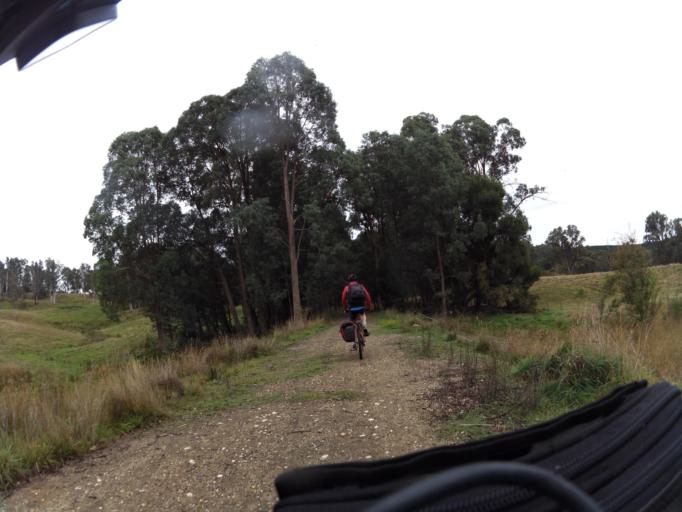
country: AU
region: New South Wales
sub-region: Greater Hume Shire
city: Holbrook
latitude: -36.1580
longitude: 147.4857
